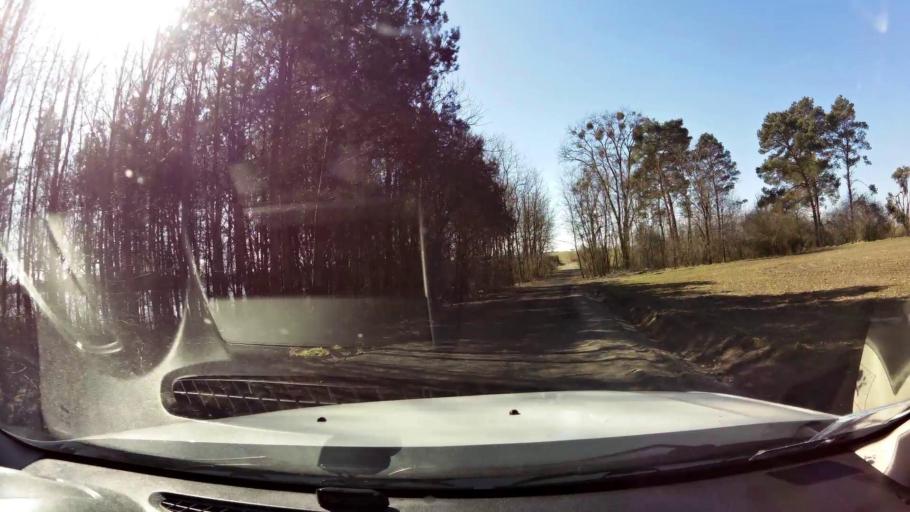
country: PL
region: West Pomeranian Voivodeship
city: Trzcinsko Zdroj
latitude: 52.9960
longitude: 14.6056
